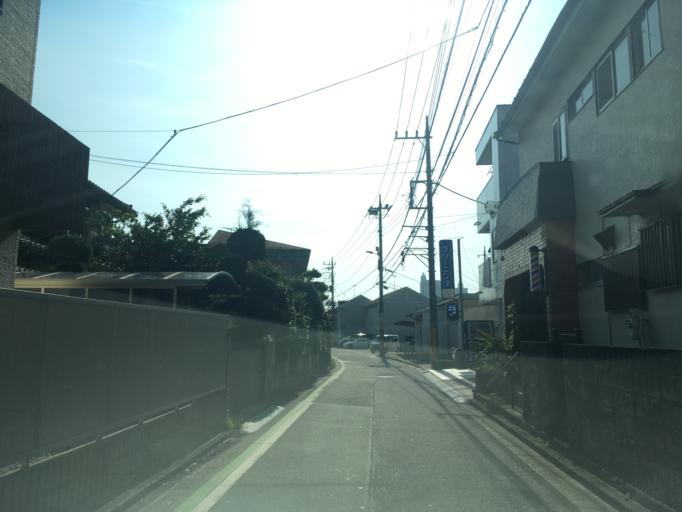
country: JP
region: Saitama
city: Tokorozawa
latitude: 35.7938
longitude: 139.4549
